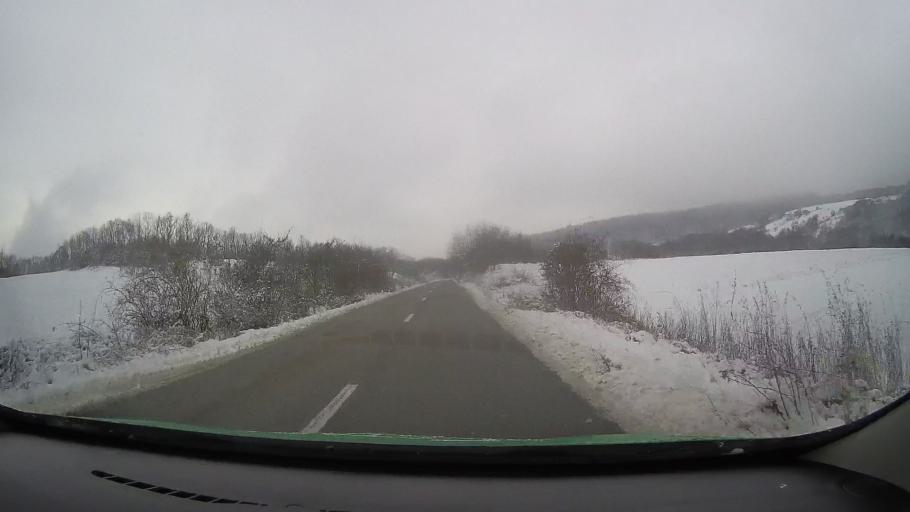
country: RO
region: Hunedoara
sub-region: Oras Hateg
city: Hateg
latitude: 45.6411
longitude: 22.9177
